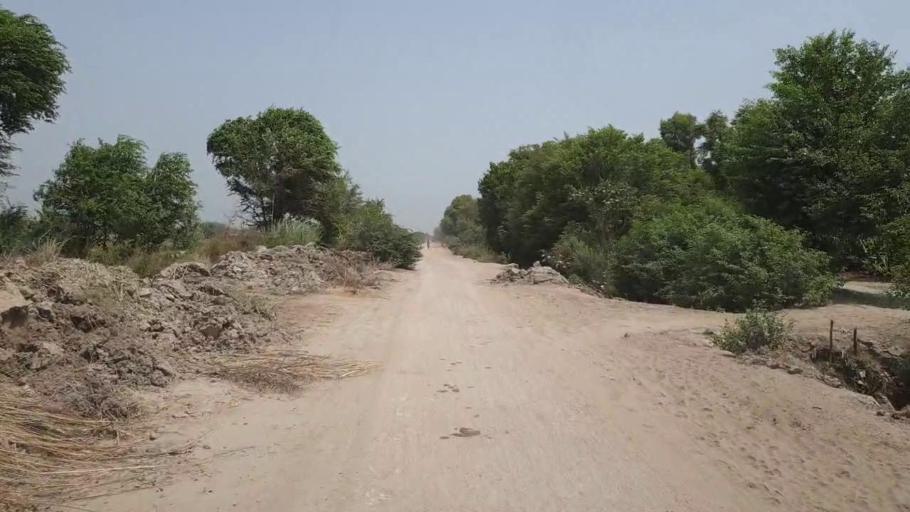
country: PK
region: Sindh
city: Nawabshah
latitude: 26.3193
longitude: 68.2984
